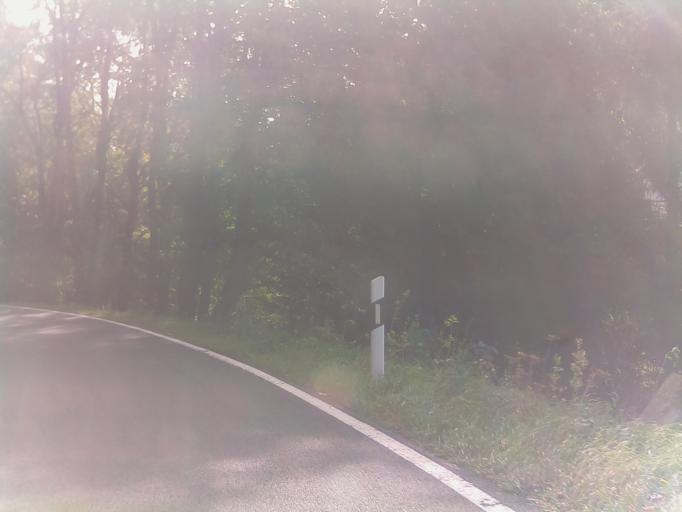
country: DE
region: Thuringia
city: Oberkatz
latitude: 50.5788
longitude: 10.2615
